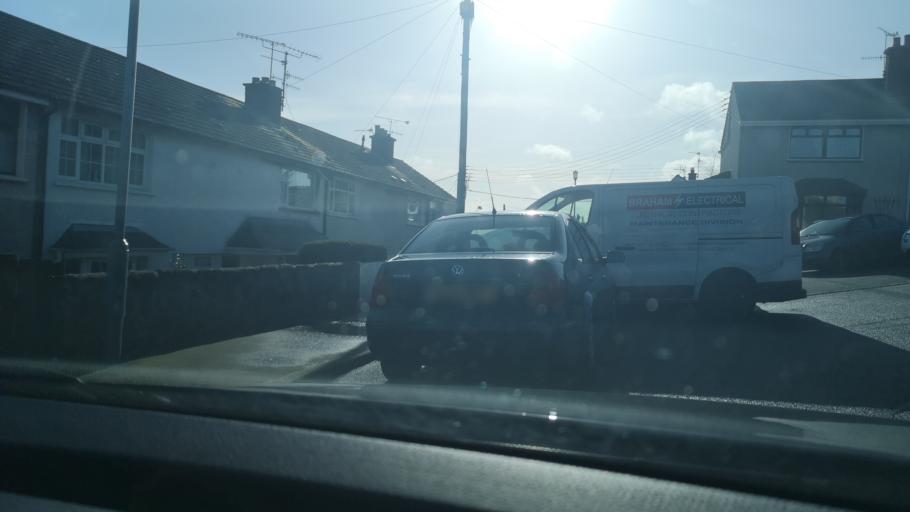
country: GB
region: Northern Ireland
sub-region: Newry and Mourne District
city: Newry
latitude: 54.1708
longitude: -6.3456
